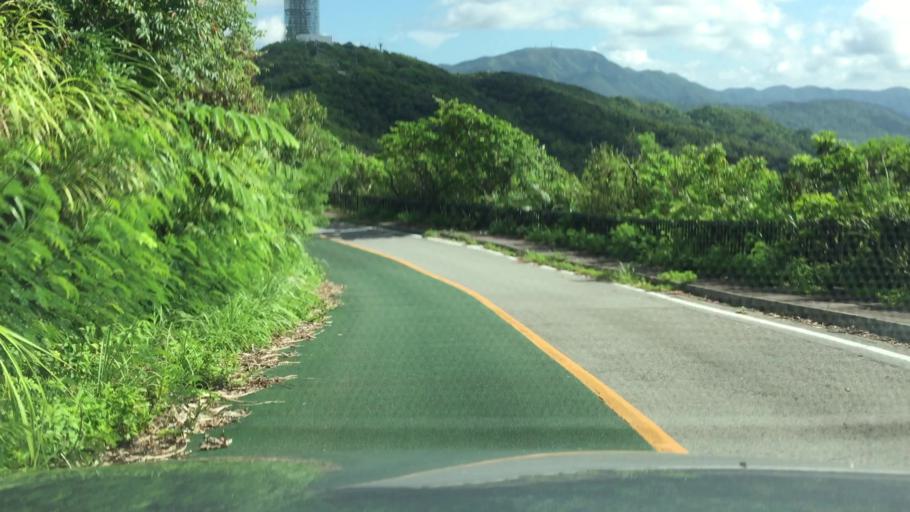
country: JP
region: Okinawa
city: Ishigaki
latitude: 24.3737
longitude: 124.1642
